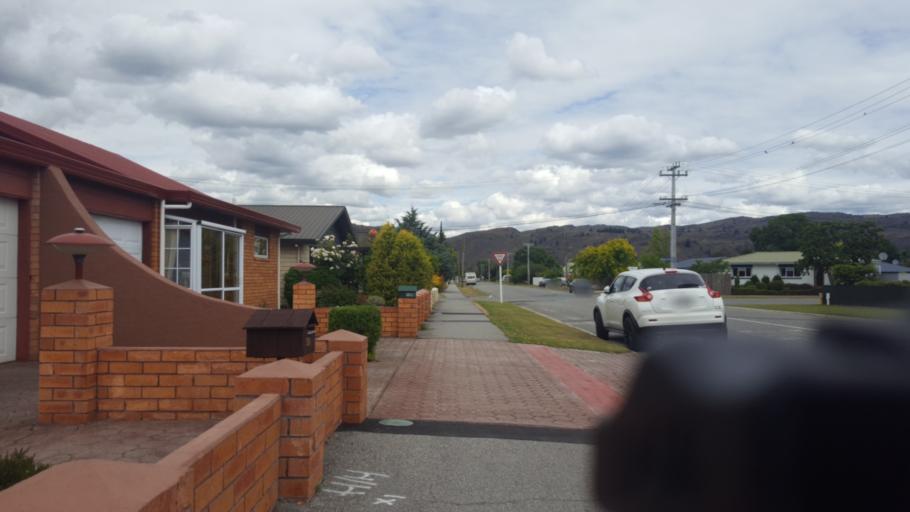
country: NZ
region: Otago
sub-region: Queenstown-Lakes District
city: Wanaka
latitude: -45.2501
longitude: 169.3849
